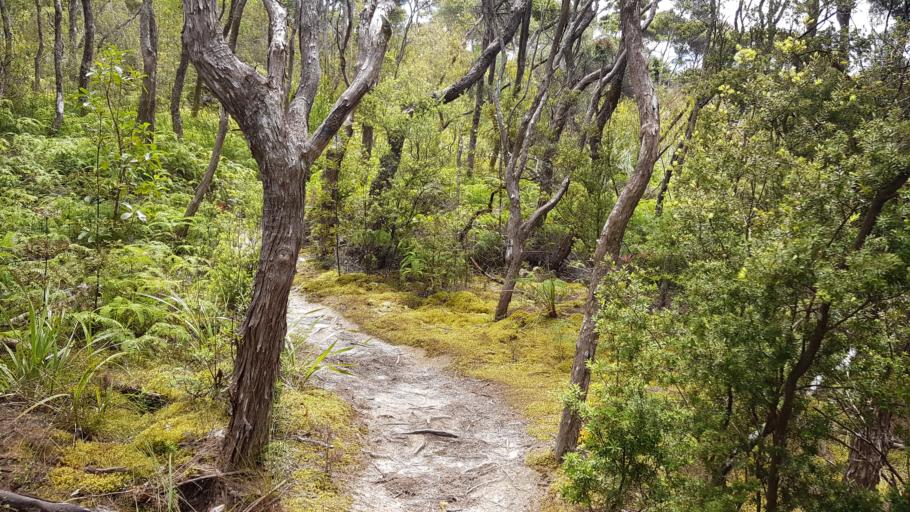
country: NZ
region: Auckland
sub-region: Auckland
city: North Shore
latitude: -36.8242
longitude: 174.7059
